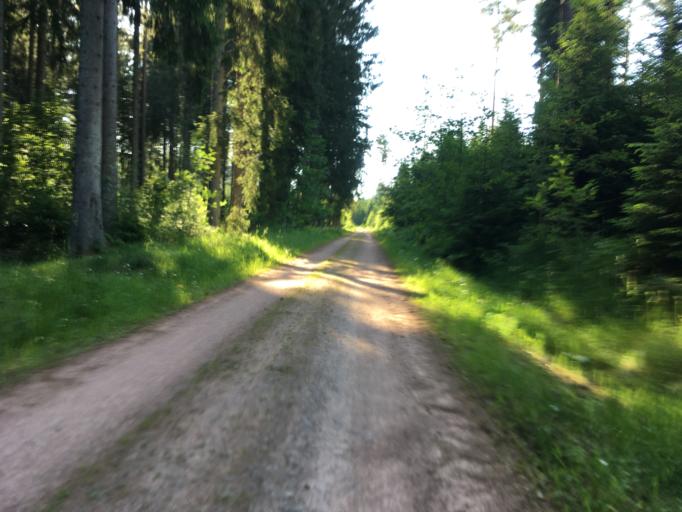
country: DE
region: Baden-Wuerttemberg
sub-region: Freiburg Region
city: Eisenbach
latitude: 47.9393
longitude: 8.2667
